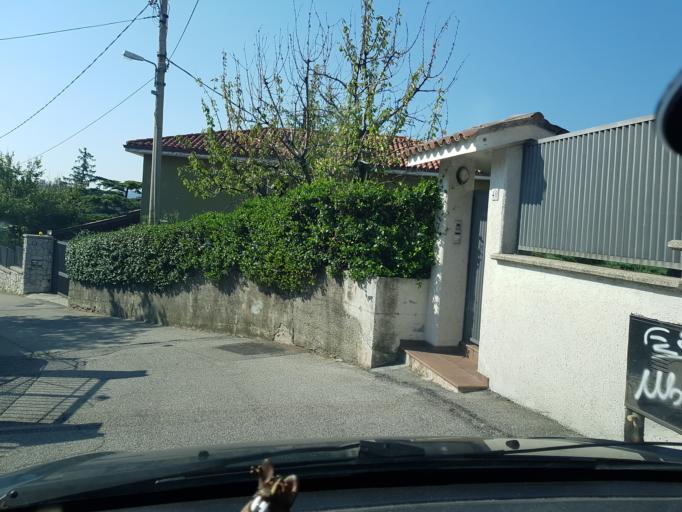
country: IT
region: Friuli Venezia Giulia
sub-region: Provincia di Trieste
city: Trieste
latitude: 45.6295
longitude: 13.8048
